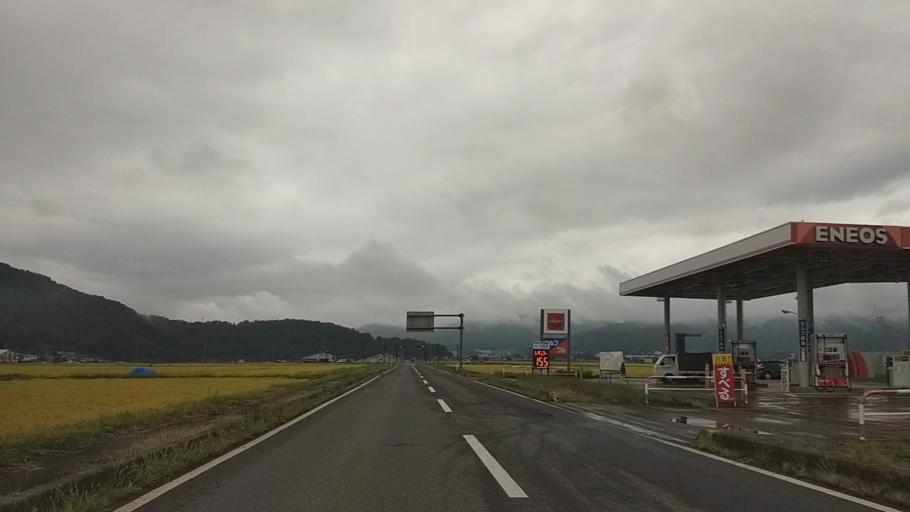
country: JP
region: Nagano
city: Iiyama
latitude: 36.8503
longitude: 138.3871
